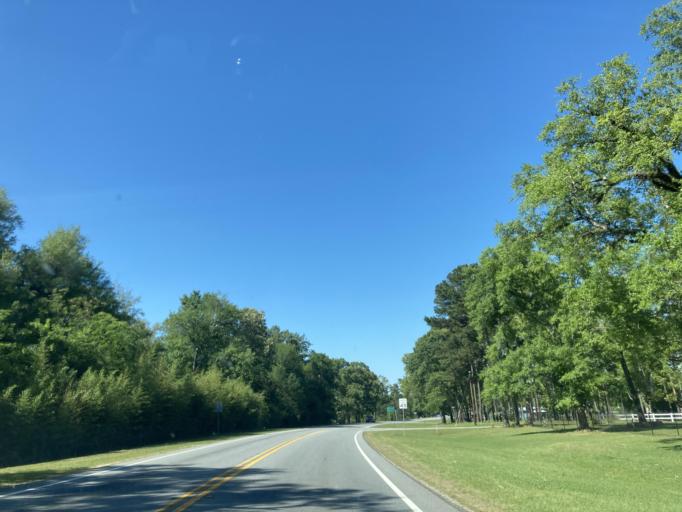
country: US
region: Georgia
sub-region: Baker County
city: Newton
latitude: 31.3169
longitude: -84.3473
